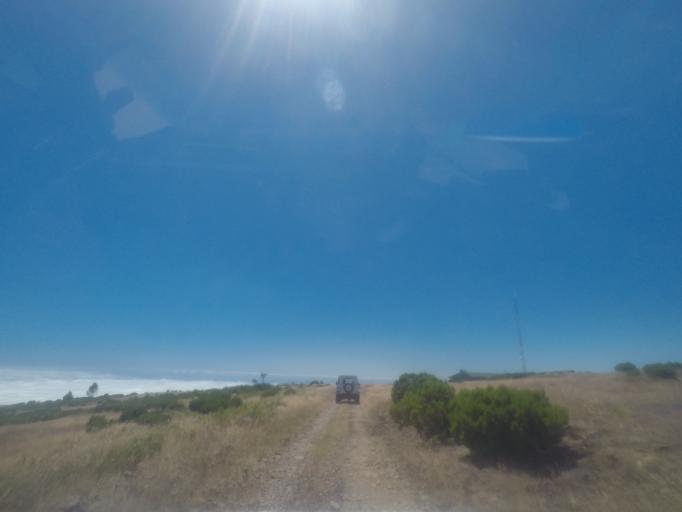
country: PT
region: Madeira
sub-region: Camara de Lobos
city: Curral das Freiras
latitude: 32.7213
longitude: -16.9159
